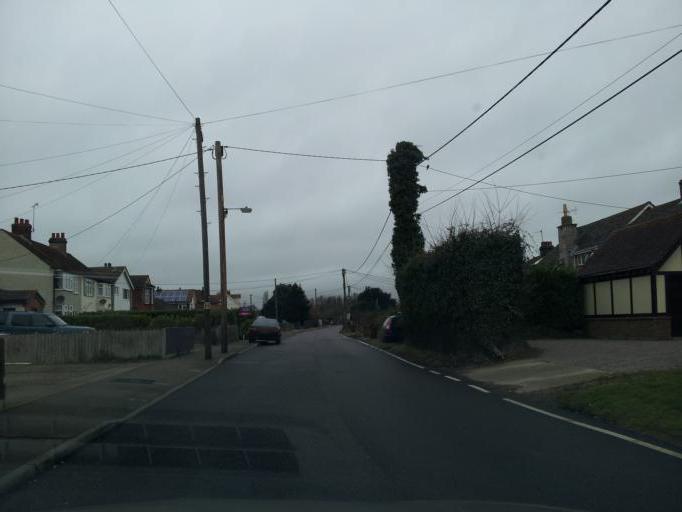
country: GB
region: England
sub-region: Essex
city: Dovercourt
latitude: 51.9250
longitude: 1.2291
